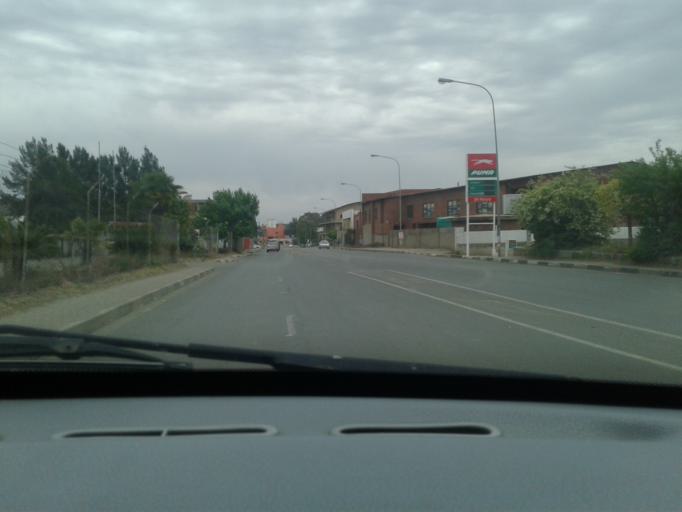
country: LS
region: Maseru
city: Maseru
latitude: -29.2987
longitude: 27.4755
